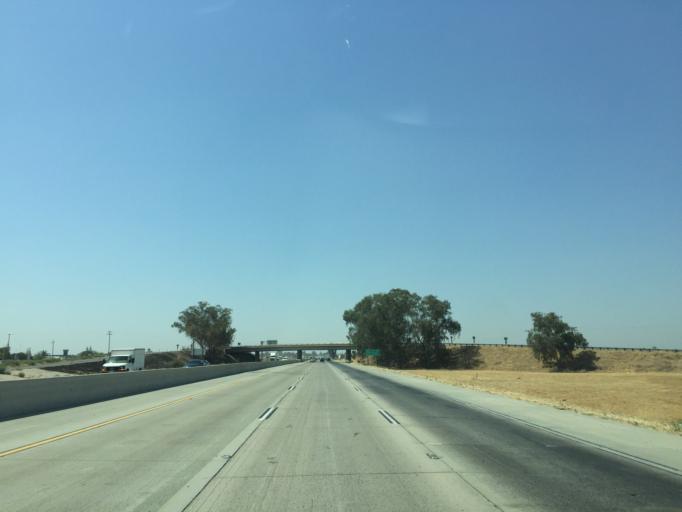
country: US
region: California
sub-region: Fresno County
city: Selma
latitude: 36.5455
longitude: -119.5942
